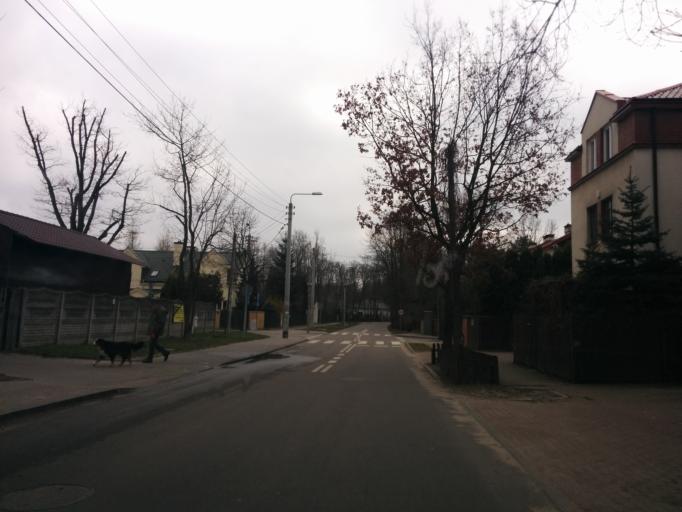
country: PL
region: Masovian Voivodeship
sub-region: Warszawa
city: Bialoleka
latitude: 52.3427
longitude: 20.9780
